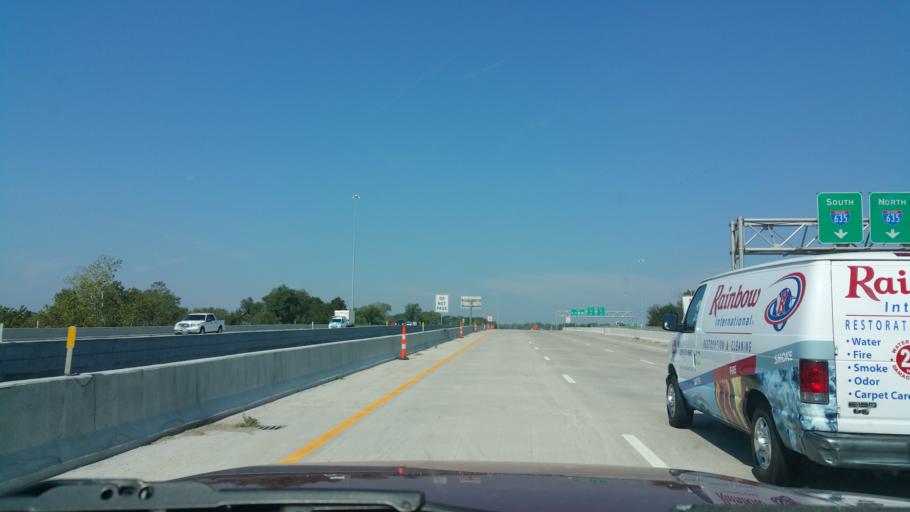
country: US
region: Kansas
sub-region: Wyandotte County
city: Kansas City
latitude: 39.1007
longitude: -94.6700
